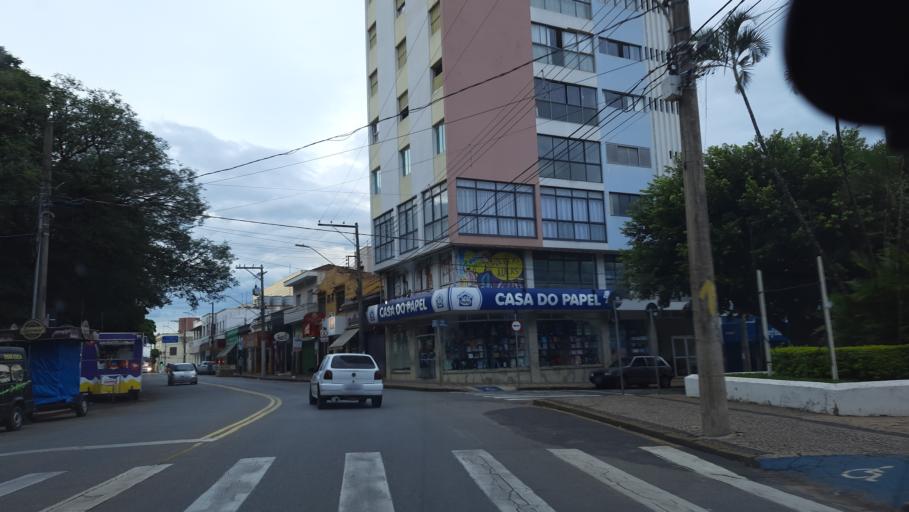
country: BR
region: Sao Paulo
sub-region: Sao Joao Da Boa Vista
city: Sao Joao da Boa Vista
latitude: -21.9709
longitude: -46.7979
